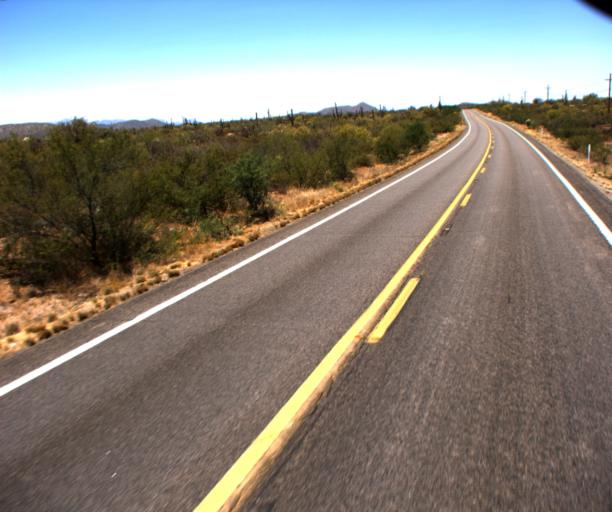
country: US
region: Arizona
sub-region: Pima County
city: Catalina
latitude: 32.6871
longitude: -111.0767
